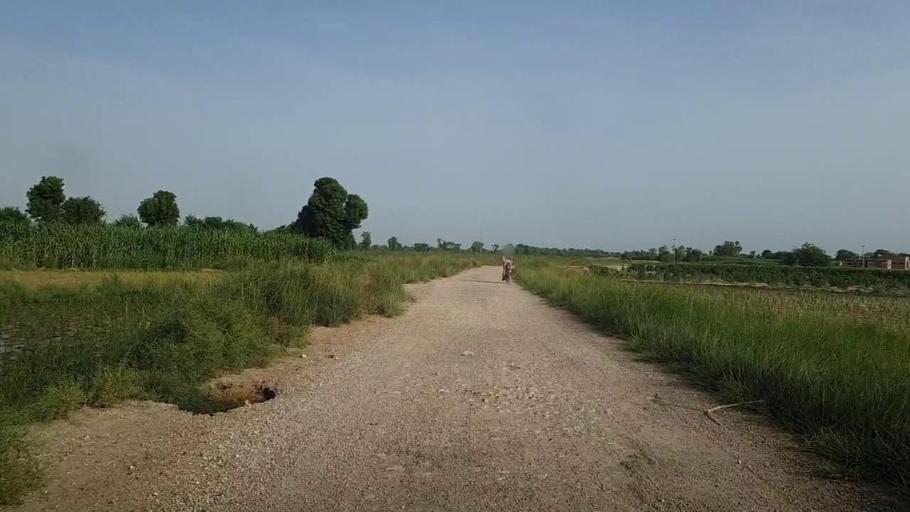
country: PK
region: Sindh
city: Pad Idan
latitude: 26.7530
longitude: 68.2571
